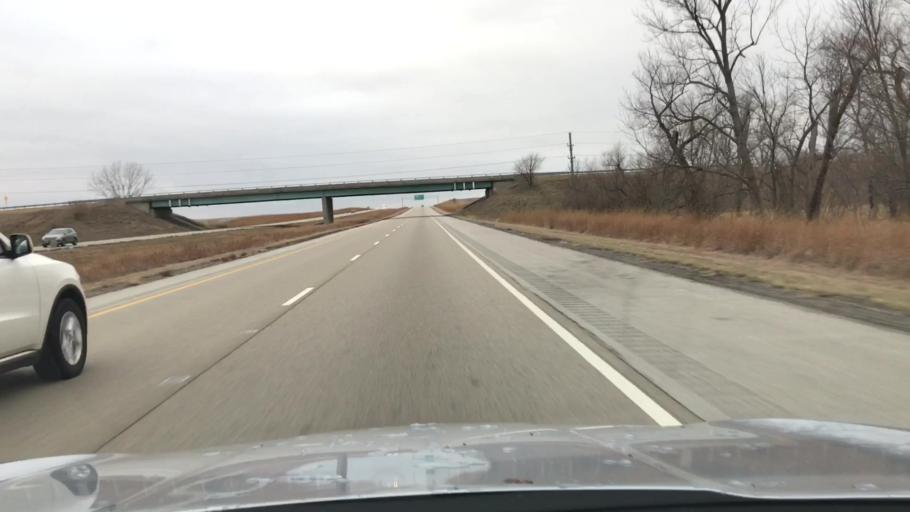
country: US
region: Illinois
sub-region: Logan County
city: Lincoln
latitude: 40.1817
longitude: -89.3854
